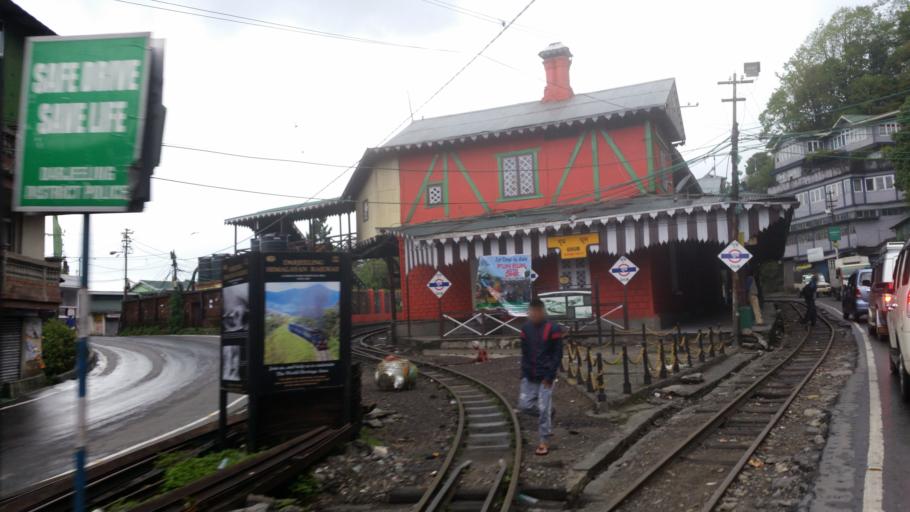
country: IN
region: West Bengal
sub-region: Darjiling
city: Darjiling
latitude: 27.0082
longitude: 88.2542
